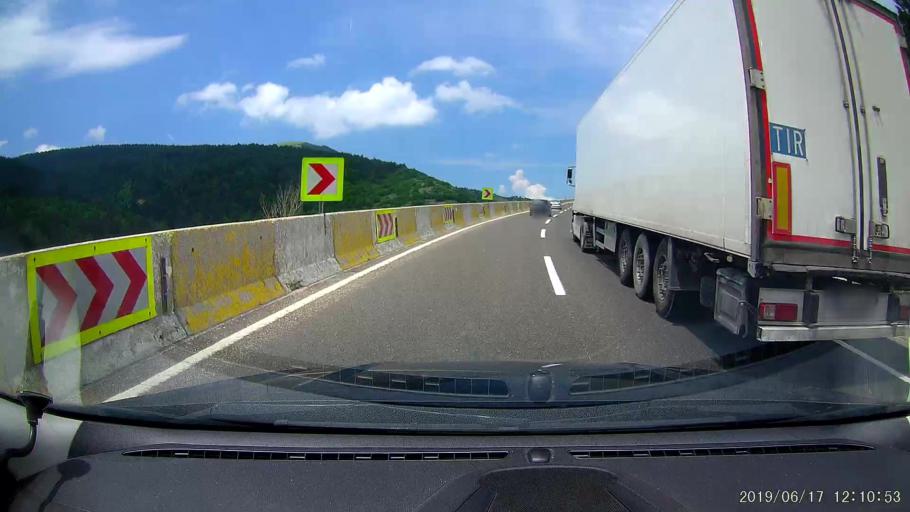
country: TR
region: Karabuk
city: Gozyeri
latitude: 40.8425
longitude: 32.6498
